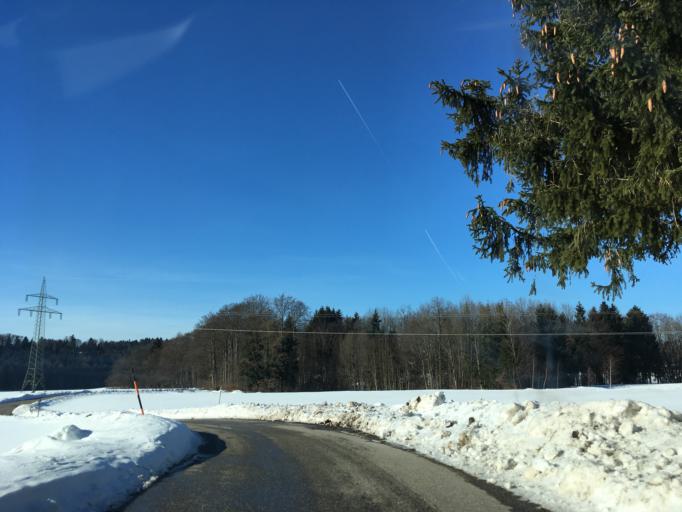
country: DE
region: Bavaria
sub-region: Upper Bavaria
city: Aschau im Chiemgau
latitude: 47.8147
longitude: 12.3332
